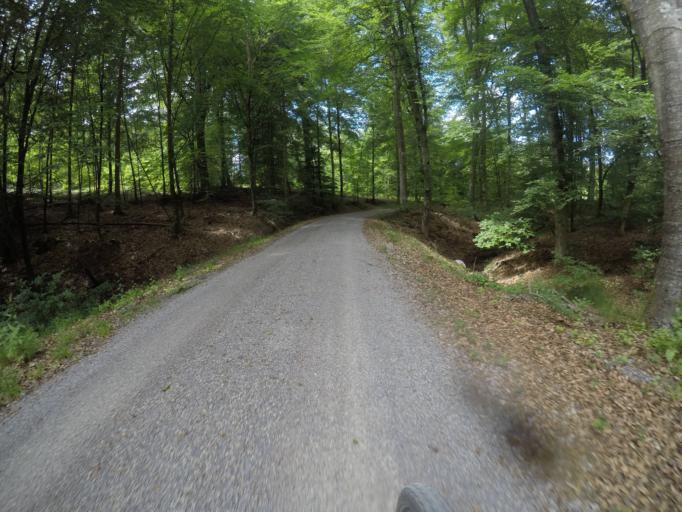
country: DE
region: Baden-Wuerttemberg
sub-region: Regierungsbezirk Stuttgart
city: Hildrizhausen
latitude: 48.6064
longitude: 8.9775
